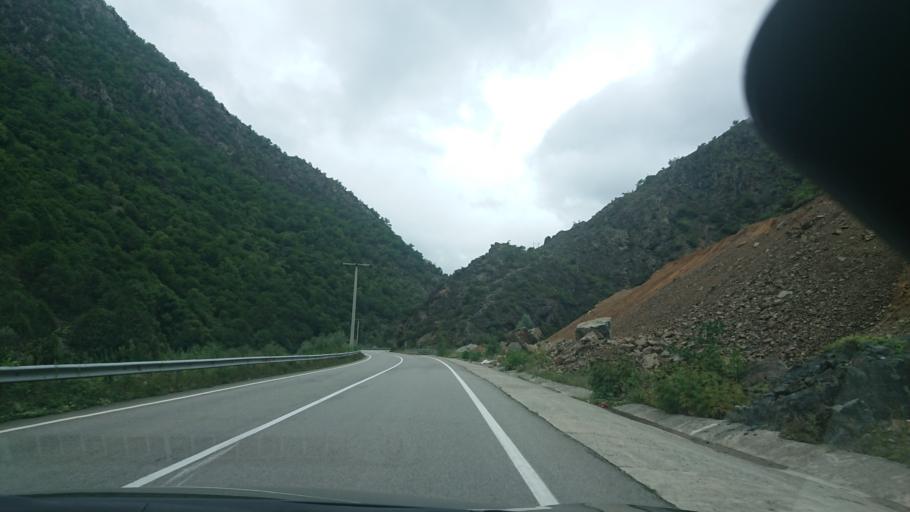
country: TR
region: Gumushane
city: Kurtun
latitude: 40.7315
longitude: 39.0132
